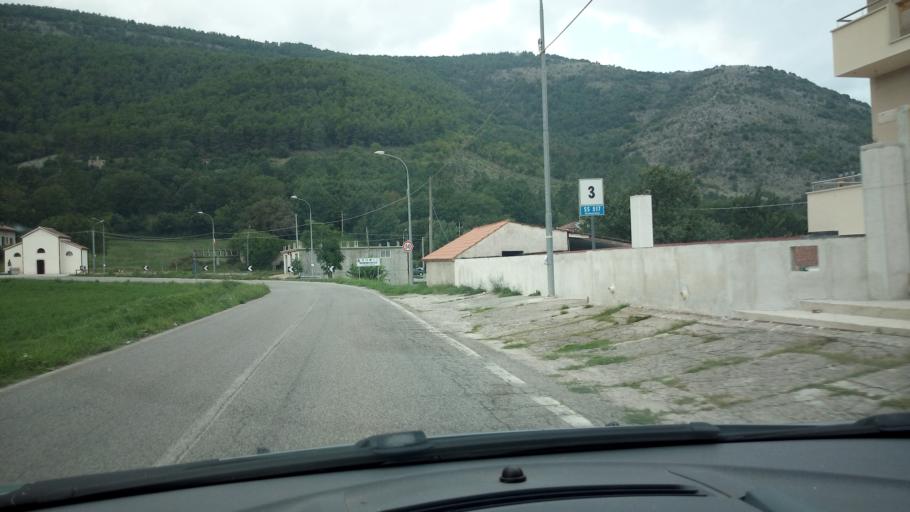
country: IT
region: Campania
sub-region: Provincia di Salerno
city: Buonabitacolo
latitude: 40.2779
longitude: 15.6265
